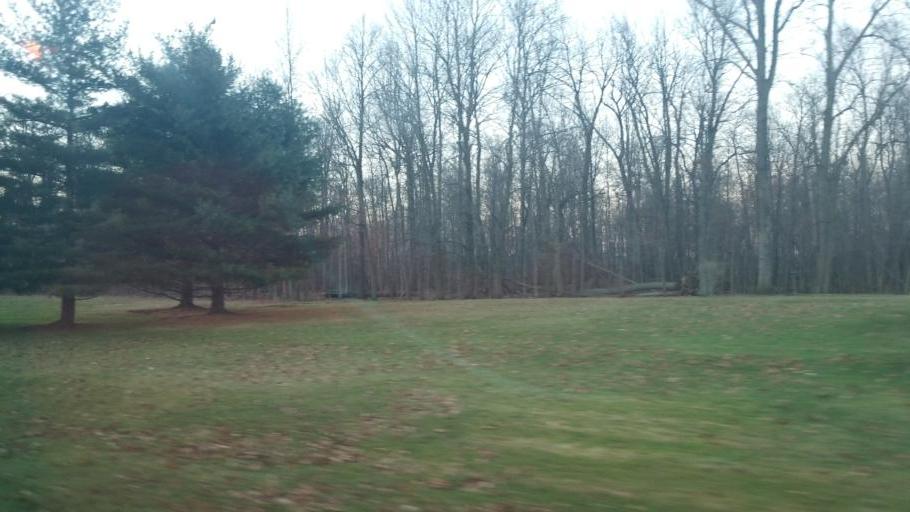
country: US
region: Ohio
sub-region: Crawford County
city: Bucyrus
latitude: 40.8265
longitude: -83.1006
